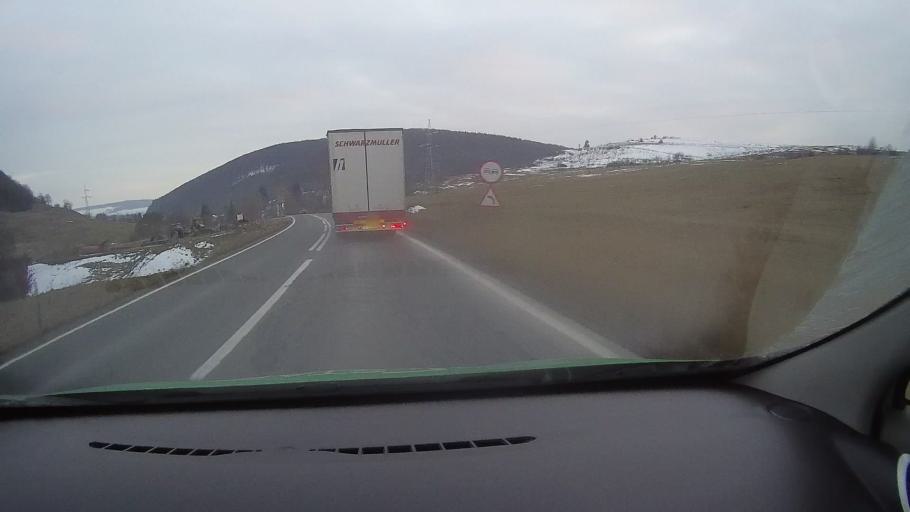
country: RO
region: Harghita
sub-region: Municipiul Odorheiu Secuiesc
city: Odorheiu Secuiesc
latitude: 46.3391
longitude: 25.2698
